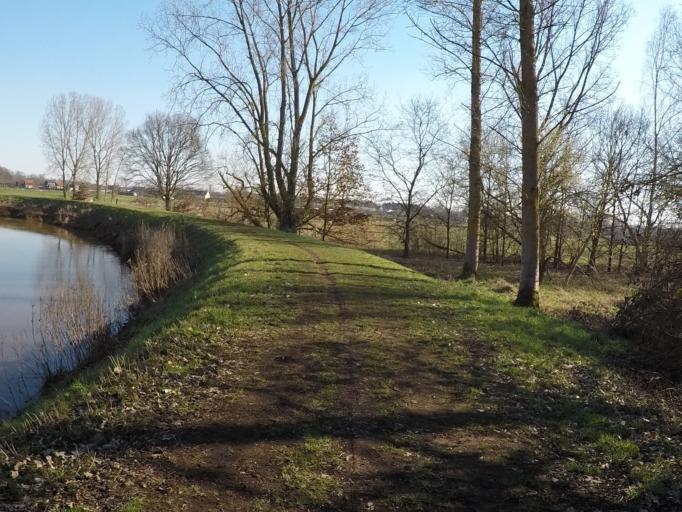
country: BE
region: Flanders
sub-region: Provincie Antwerpen
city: Heist-op-den-Berg
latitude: 51.1080
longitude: 4.7371
